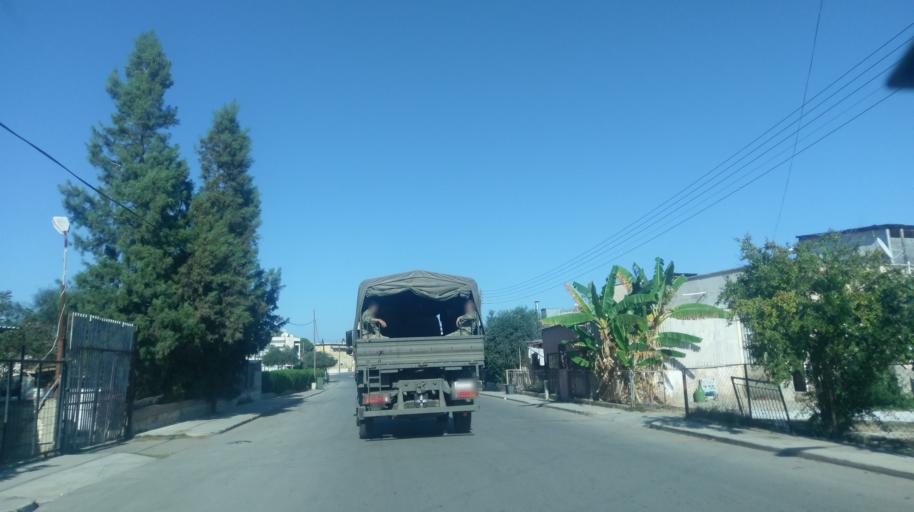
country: CY
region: Ammochostos
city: Famagusta
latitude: 35.1048
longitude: 33.9478
